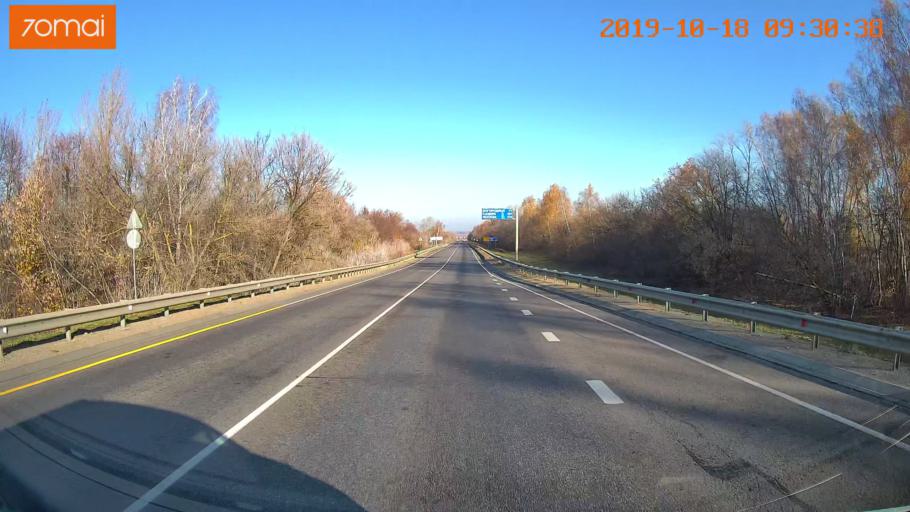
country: RU
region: Tula
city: Yefremov
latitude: 53.1404
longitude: 38.1595
